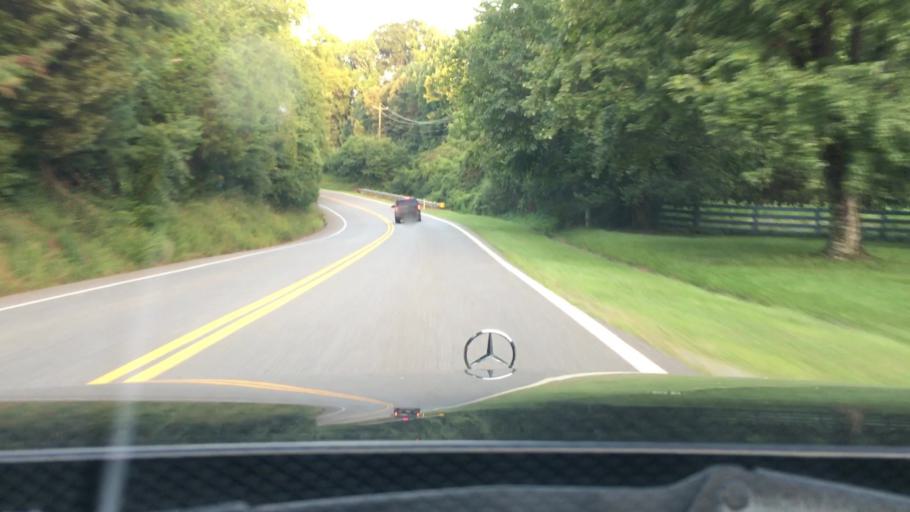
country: US
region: Virginia
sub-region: Campbell County
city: Altavista
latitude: 37.1291
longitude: -79.2783
